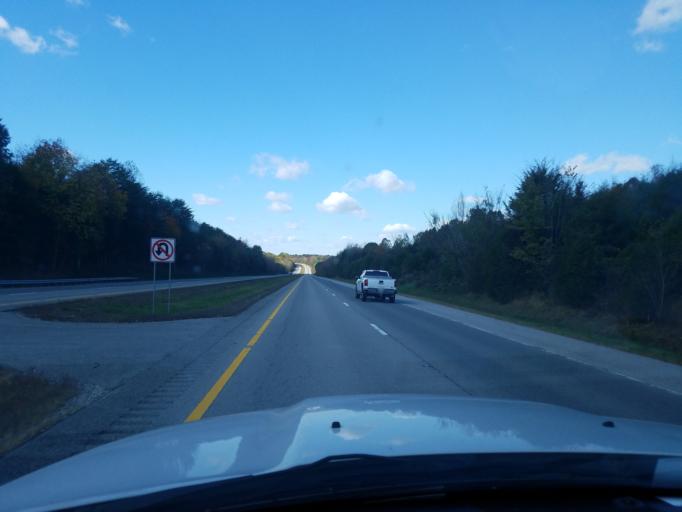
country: US
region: Kentucky
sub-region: Barren County
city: Glasgow
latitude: 36.9963
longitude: -85.7791
